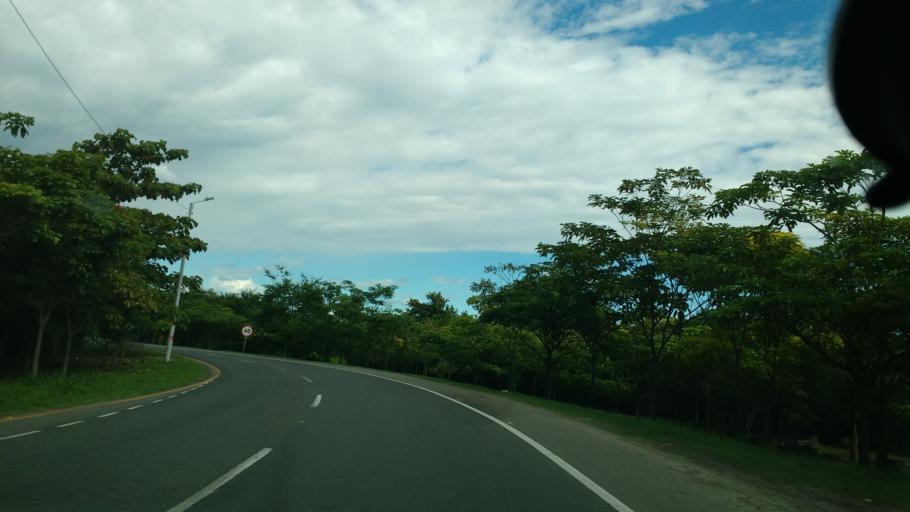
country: CO
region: Tolima
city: Valle de San Juan
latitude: 4.3266
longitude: -75.0770
